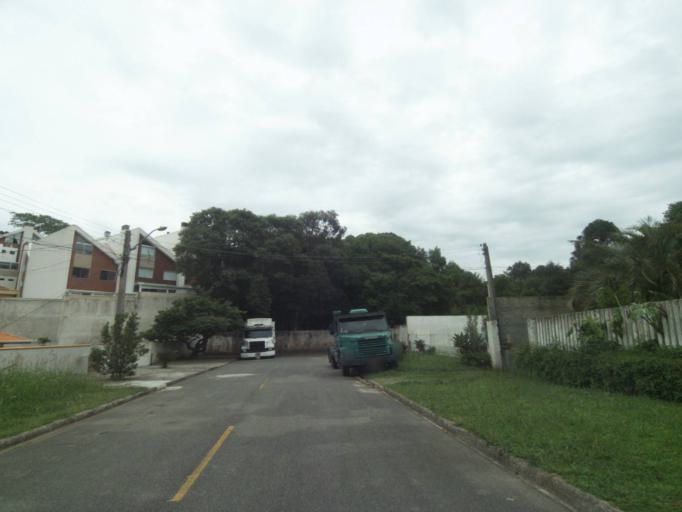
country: BR
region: Parana
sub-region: Curitiba
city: Curitiba
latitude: -25.3958
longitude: -49.2909
